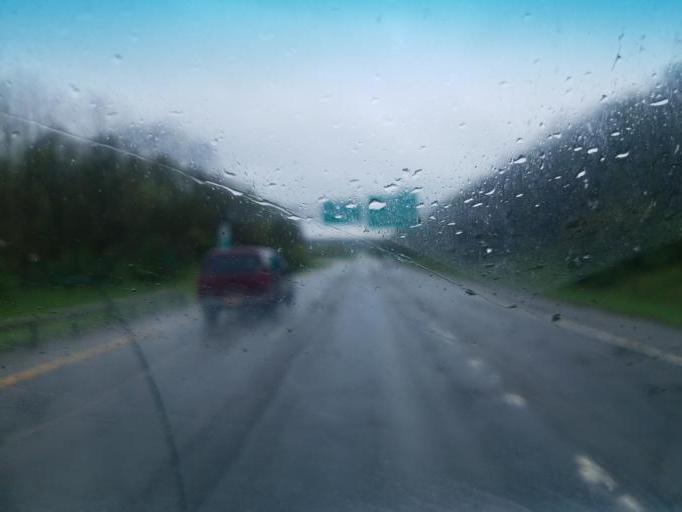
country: US
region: New York
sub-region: Chautauqua County
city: Lakewood
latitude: 42.1508
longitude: -79.3668
